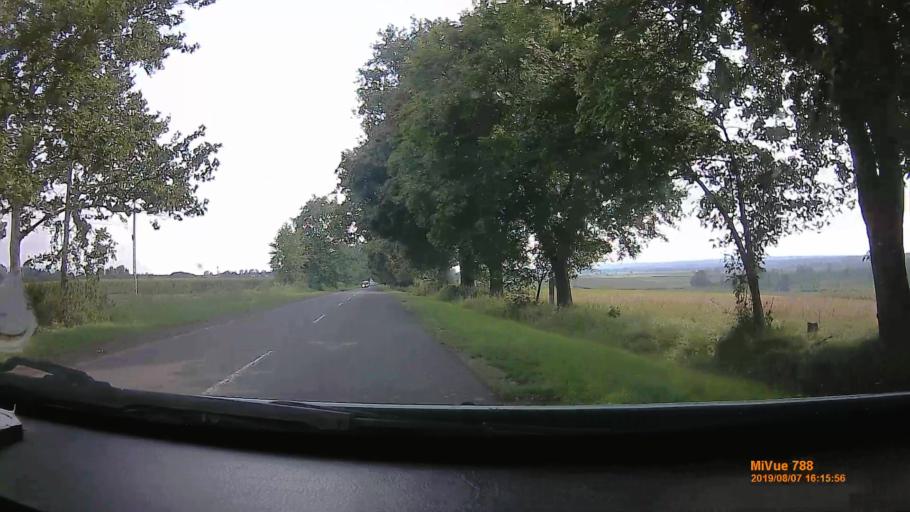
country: HU
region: Borsod-Abauj-Zemplen
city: Gonc
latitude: 48.4660
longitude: 21.2523
